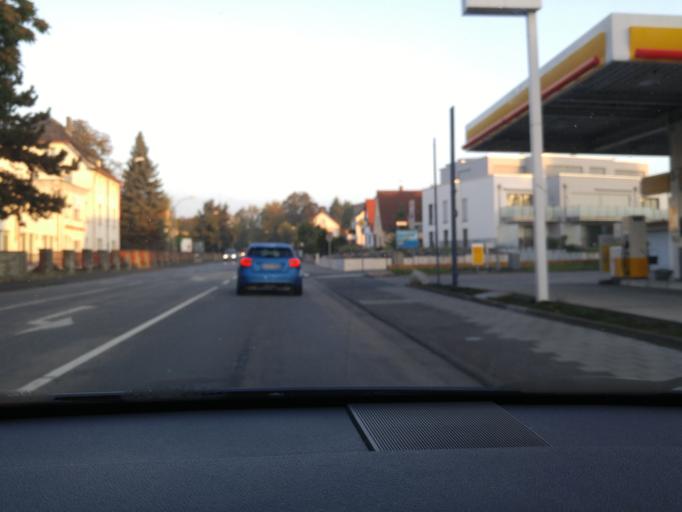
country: DE
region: Hesse
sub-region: Regierungsbezirk Darmstadt
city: Bad Nauheim
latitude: 50.3757
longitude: 8.7400
